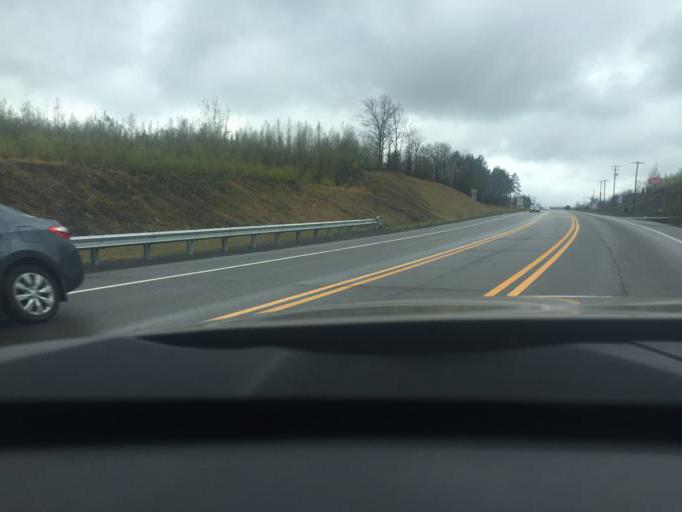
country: US
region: Pennsylvania
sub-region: Luzerne County
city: Harleigh
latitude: 40.9924
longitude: -75.9971
